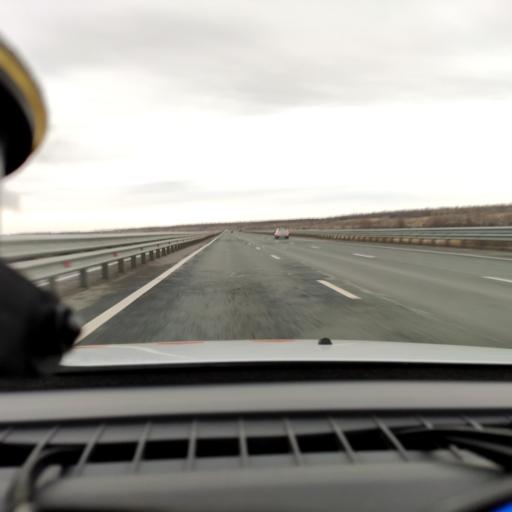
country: RU
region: Samara
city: Smyshlyayevka
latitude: 53.1556
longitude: 50.3422
